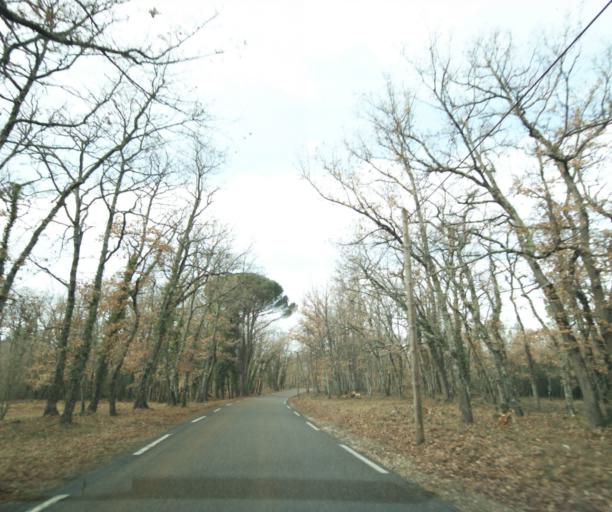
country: FR
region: Provence-Alpes-Cote d'Azur
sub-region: Departement du Var
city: Rougiers
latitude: 43.3933
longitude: 5.8884
